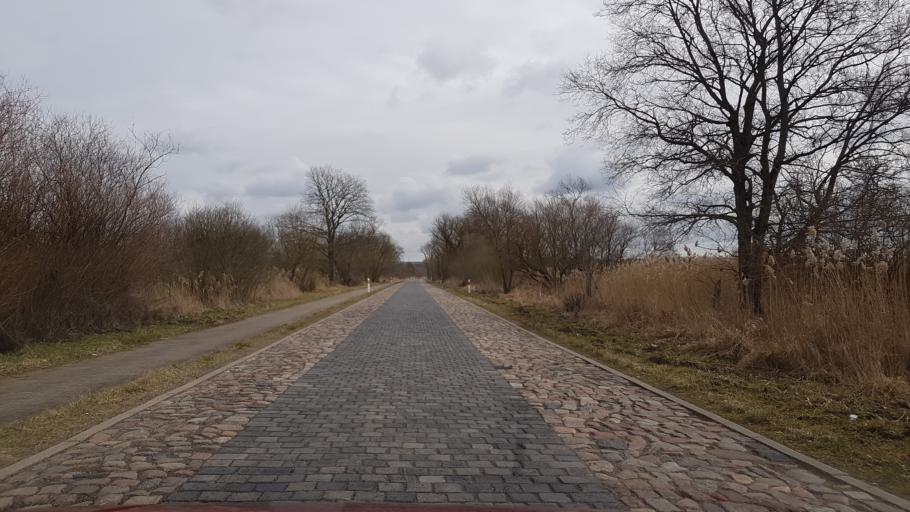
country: PL
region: West Pomeranian Voivodeship
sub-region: Powiat gryfinski
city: Gryfino
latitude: 53.2539
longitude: 14.4629
